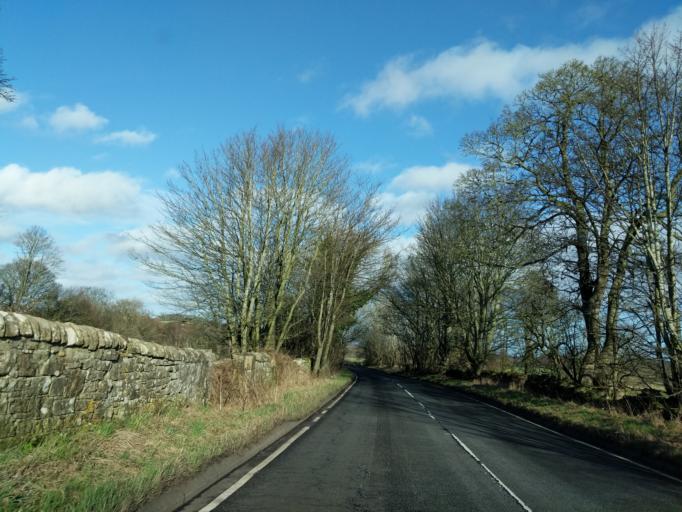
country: GB
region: Scotland
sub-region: West Lothian
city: Kirknewton
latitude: 55.8944
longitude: -3.3988
